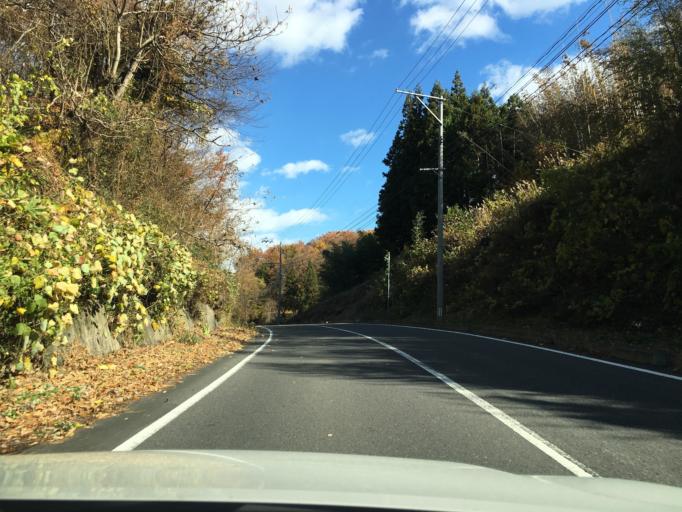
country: JP
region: Fukushima
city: Miharu
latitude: 37.4457
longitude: 140.4647
